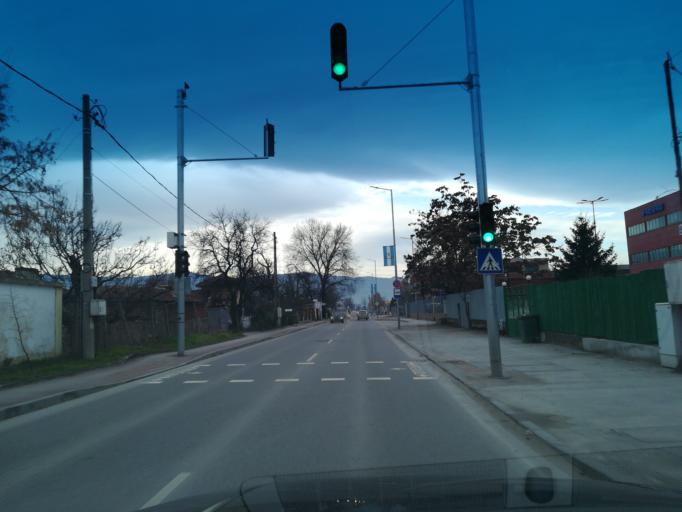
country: BG
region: Plovdiv
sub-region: Obshtina Plovdiv
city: Plovdiv
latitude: 42.1224
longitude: 24.7174
